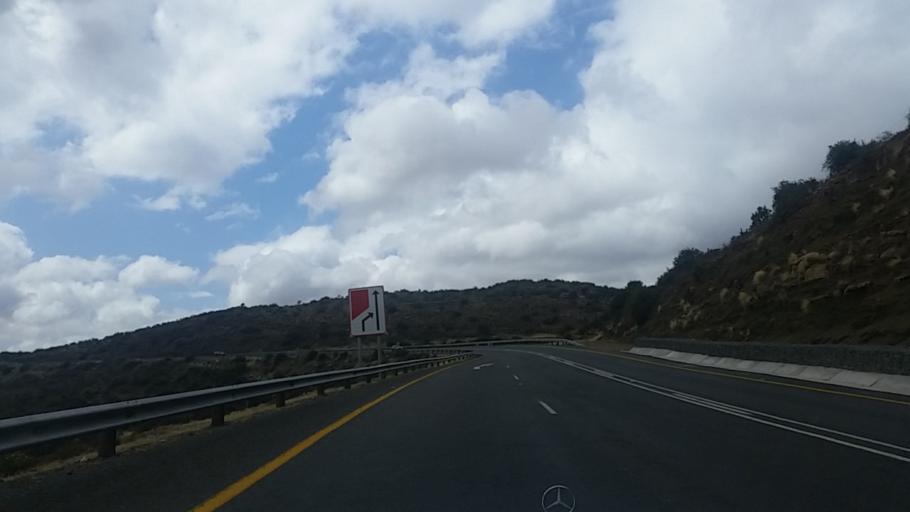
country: ZA
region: Eastern Cape
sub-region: Cacadu District Municipality
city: Graaff-Reinet
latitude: -32.1133
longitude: 24.6086
